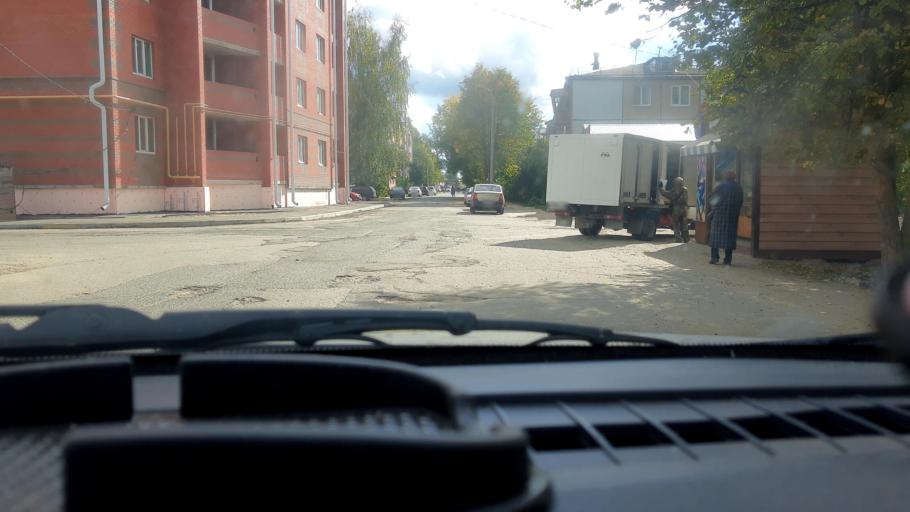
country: RU
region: Mariy-El
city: Medvedevo
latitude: 56.6362
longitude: 47.7979
